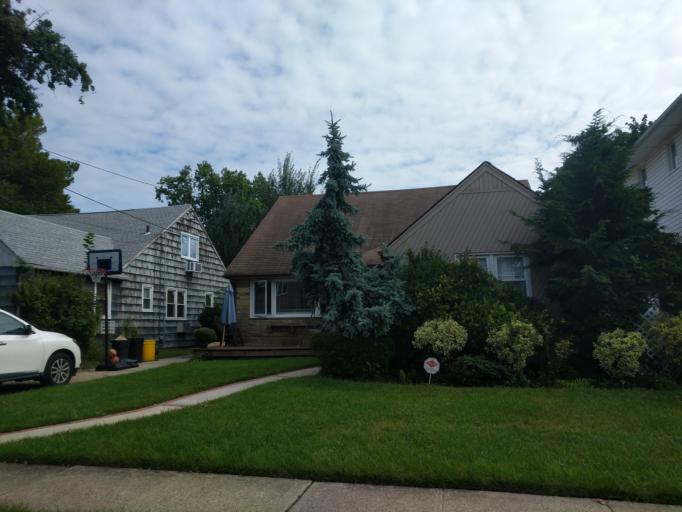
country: US
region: New York
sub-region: Nassau County
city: Cedarhurst
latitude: 40.6281
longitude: -73.7334
